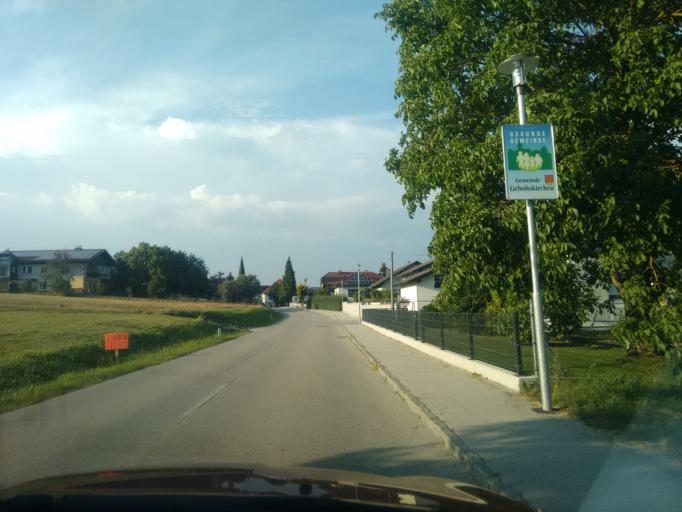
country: AT
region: Upper Austria
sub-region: Politischer Bezirk Vocklabruck
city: Wolfsegg am Hausruck
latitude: 48.1499
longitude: 13.6328
